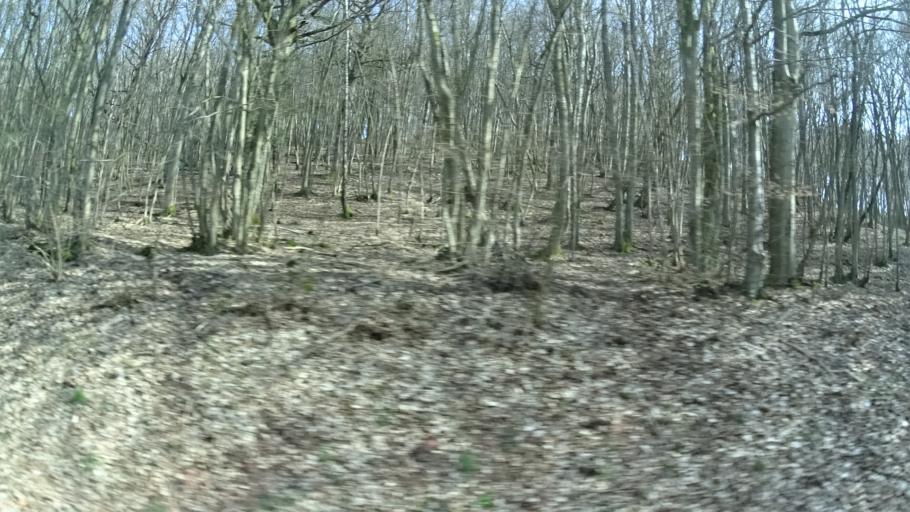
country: DE
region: Rheinland-Pfalz
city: Gimbweiler
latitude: 49.5986
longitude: 7.1944
